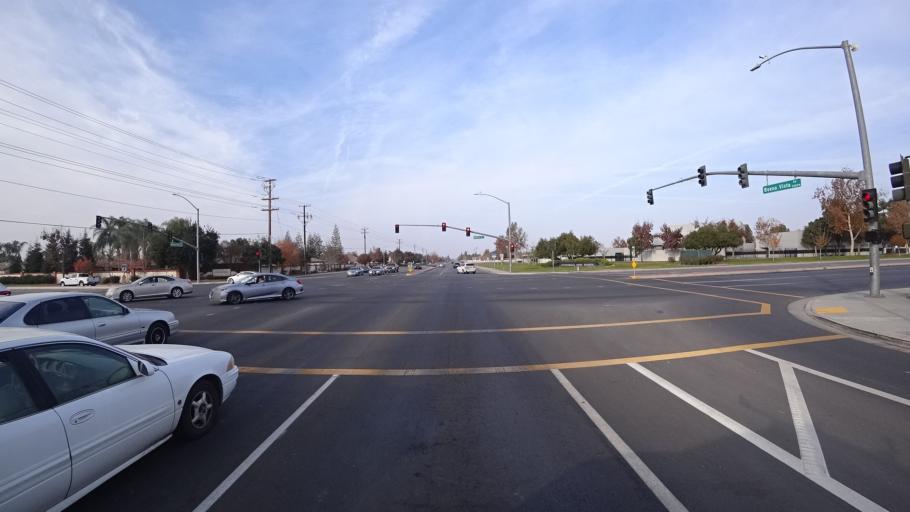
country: US
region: California
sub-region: Kern County
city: Greenacres
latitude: 35.3250
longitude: -119.1279
